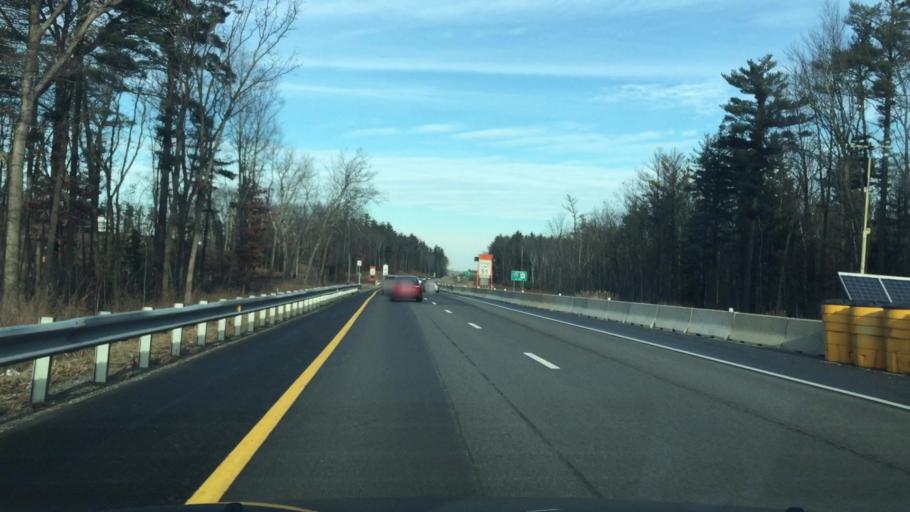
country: US
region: New Hampshire
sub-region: Rockingham County
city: Londonderry
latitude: 42.9257
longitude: -71.3775
